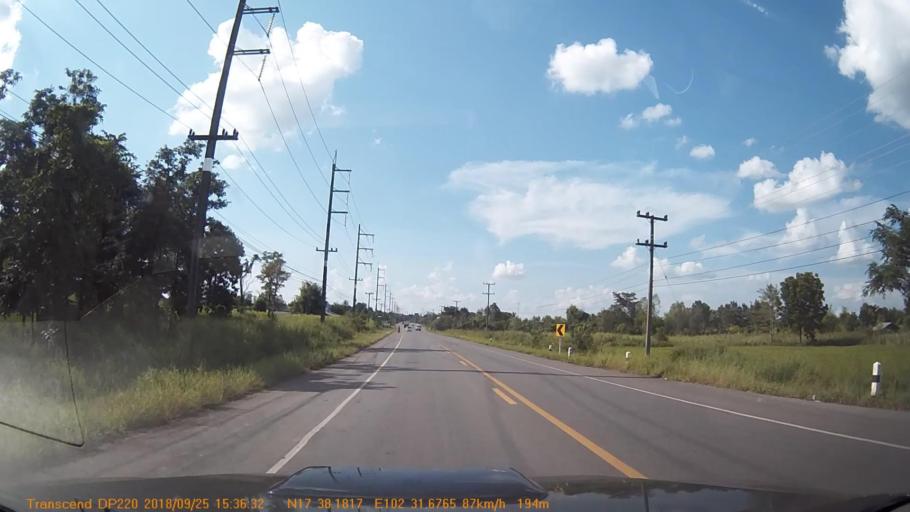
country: TH
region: Changwat Udon Thani
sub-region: Amphoe Ban Phue
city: Ban Phue
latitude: 17.6367
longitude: 102.5278
